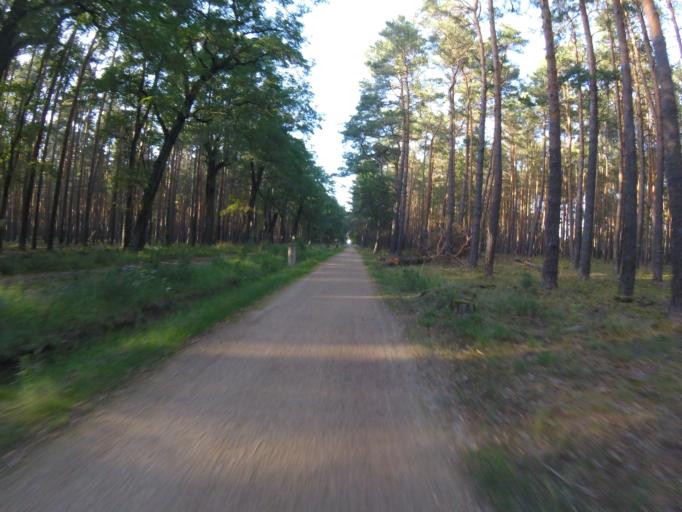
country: DE
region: Brandenburg
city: Munchehofe
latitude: 52.2115
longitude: 13.7715
